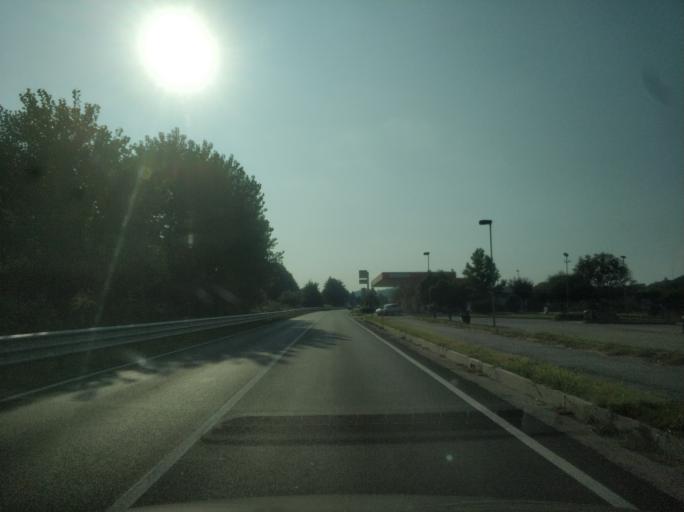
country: IT
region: Piedmont
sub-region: Provincia di Cuneo
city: Cinzano
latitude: 44.6951
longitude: 7.9034
